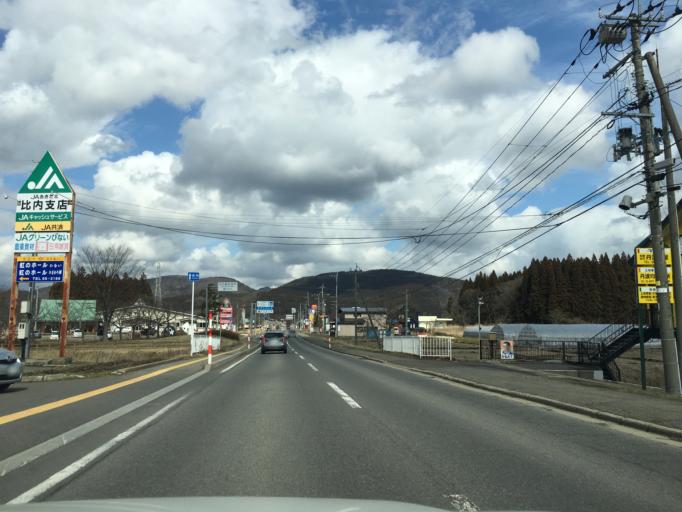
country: JP
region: Akita
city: Odate
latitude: 40.2177
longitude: 140.5850
